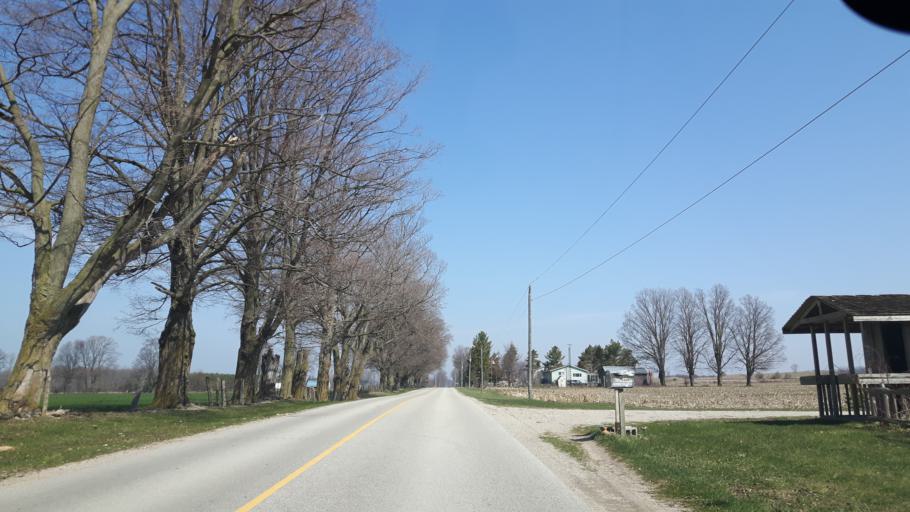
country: CA
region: Ontario
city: Goderich
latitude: 43.6696
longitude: -81.6846
